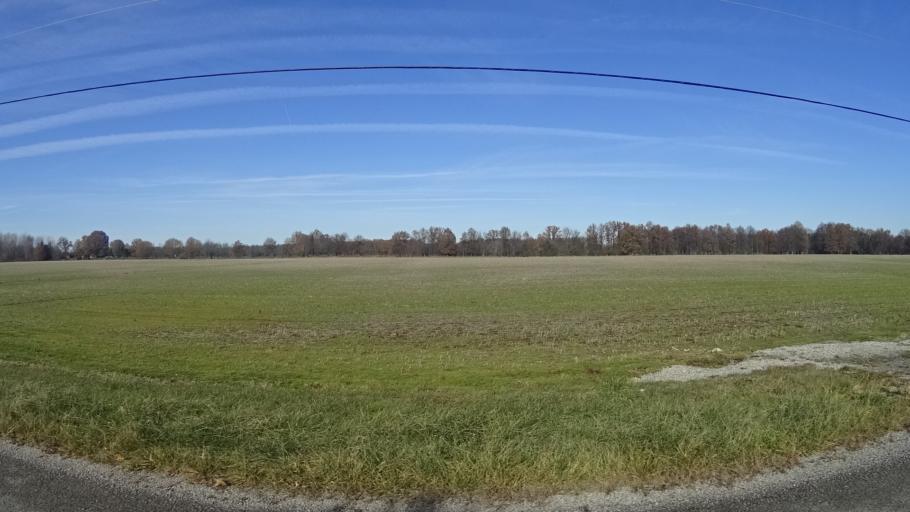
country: US
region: Ohio
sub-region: Lorain County
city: Eaton Estates
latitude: 41.3405
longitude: -81.9851
